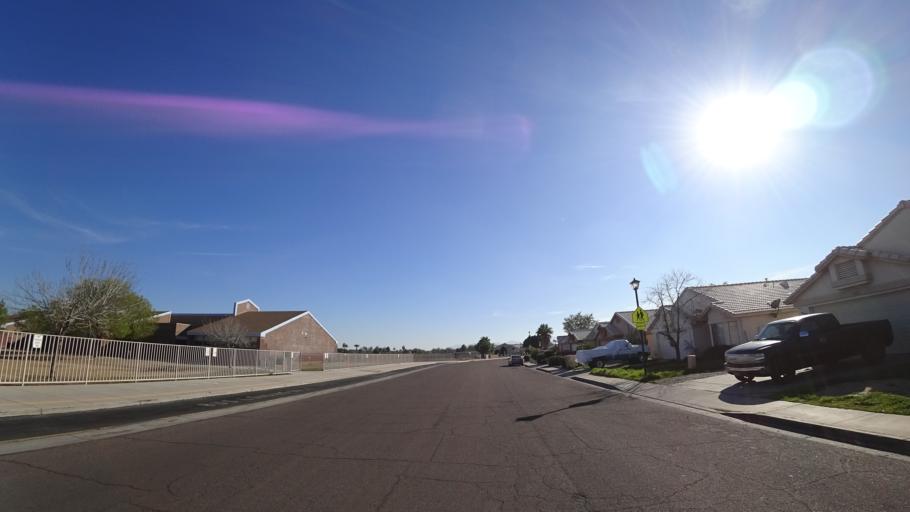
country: US
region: Arizona
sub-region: Maricopa County
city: Glendale
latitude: 33.5226
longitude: -112.2249
